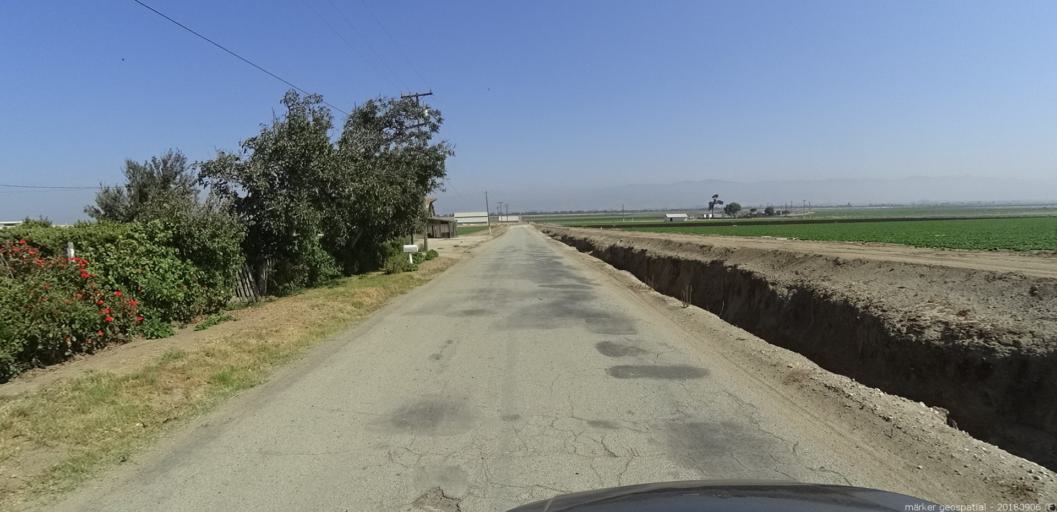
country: US
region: California
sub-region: Monterey County
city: Chualar
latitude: 36.5932
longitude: -121.6028
